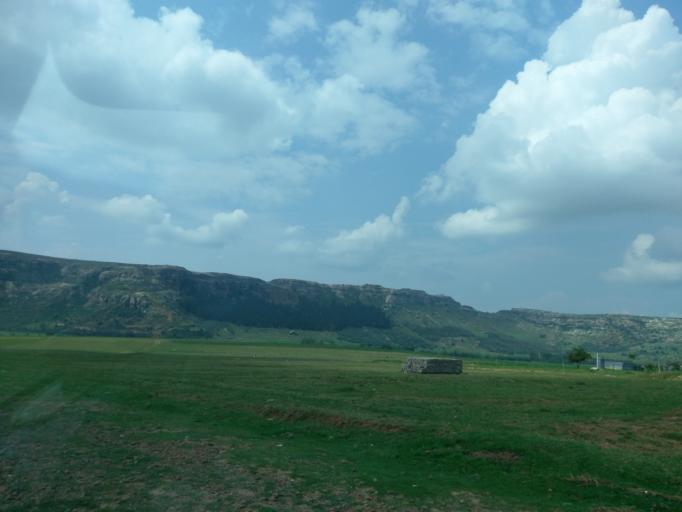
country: LS
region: Leribe
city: Leribe
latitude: -29.0211
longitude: 28.0165
